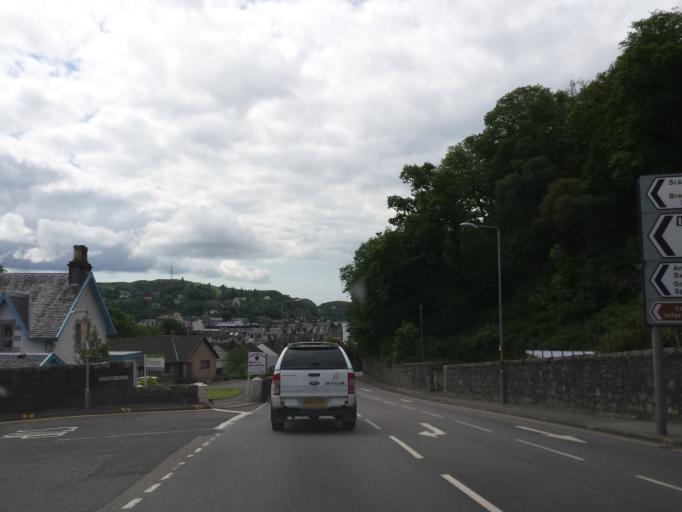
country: GB
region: Scotland
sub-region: Argyll and Bute
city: Oban
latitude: 56.4205
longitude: -5.4720
